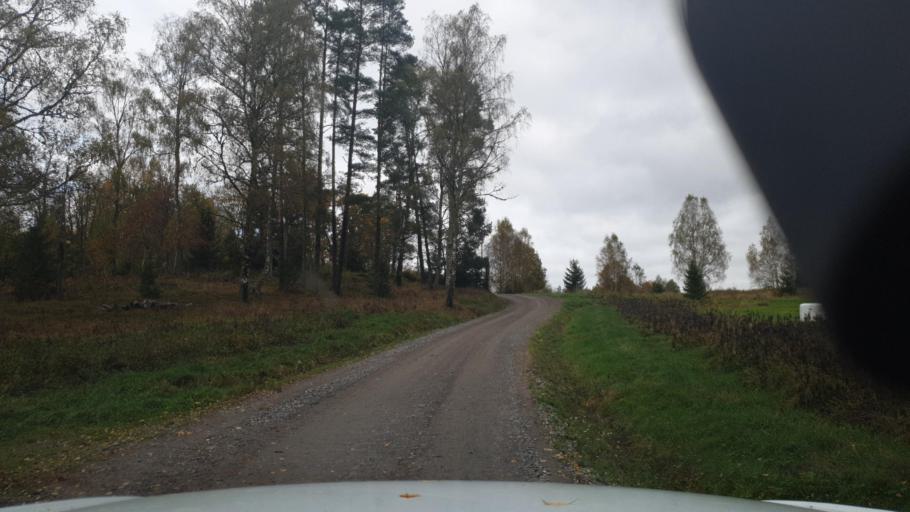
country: SE
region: Vaermland
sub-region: Karlstads Kommun
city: Edsvalla
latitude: 59.4711
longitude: 13.1272
